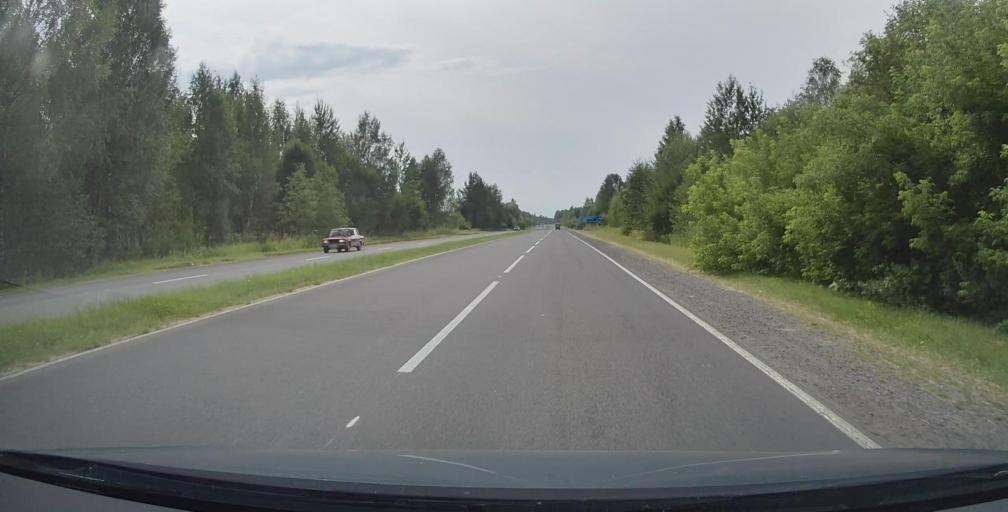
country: RU
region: Jaroslavl
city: Rybinsk
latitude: 58.0092
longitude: 38.9171
